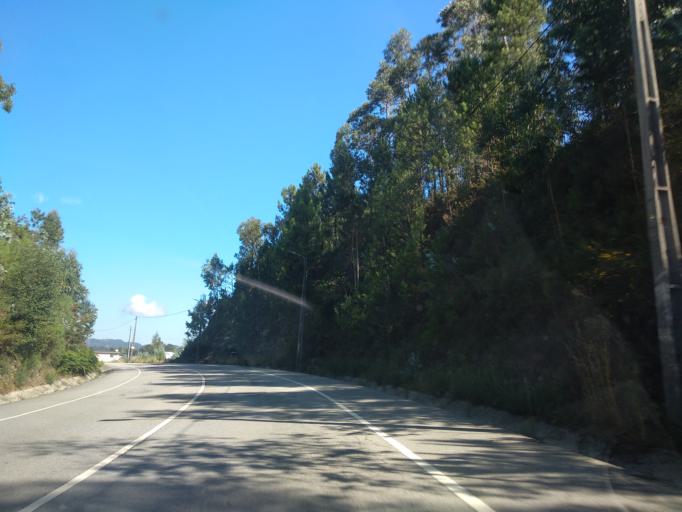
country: PT
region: Porto
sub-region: Pacos de Ferreira
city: Ferreira
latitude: 41.2671
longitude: -8.3333
